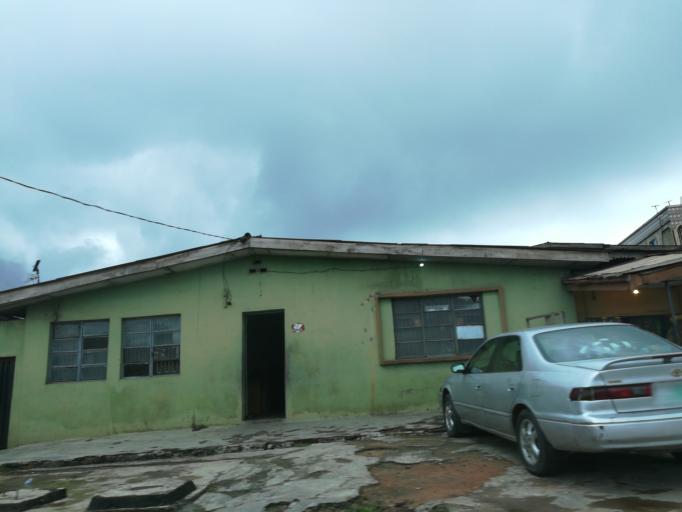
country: NG
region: Lagos
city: Agege
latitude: 6.6121
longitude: 3.3267
